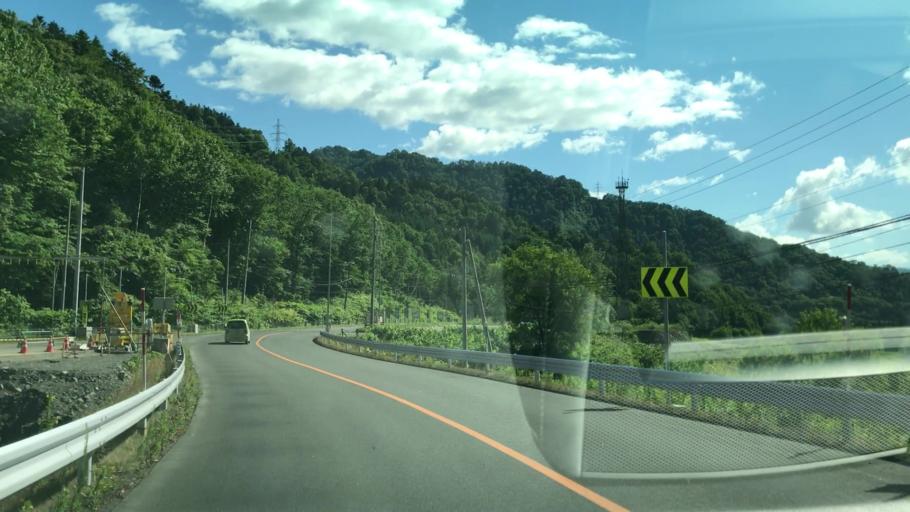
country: JP
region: Hokkaido
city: Shimo-furano
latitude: 42.9107
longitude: 142.5851
